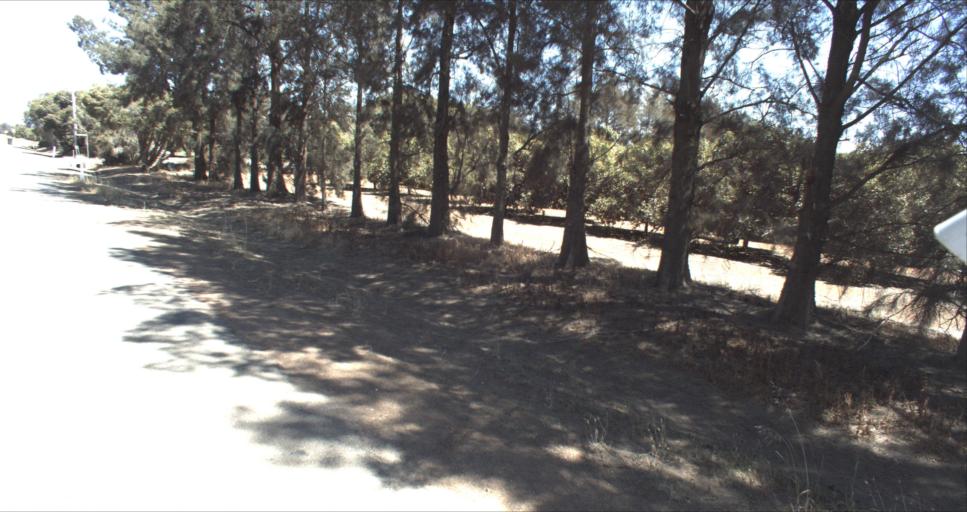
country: AU
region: New South Wales
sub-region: Leeton
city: Leeton
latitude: -34.5299
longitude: 146.3292
